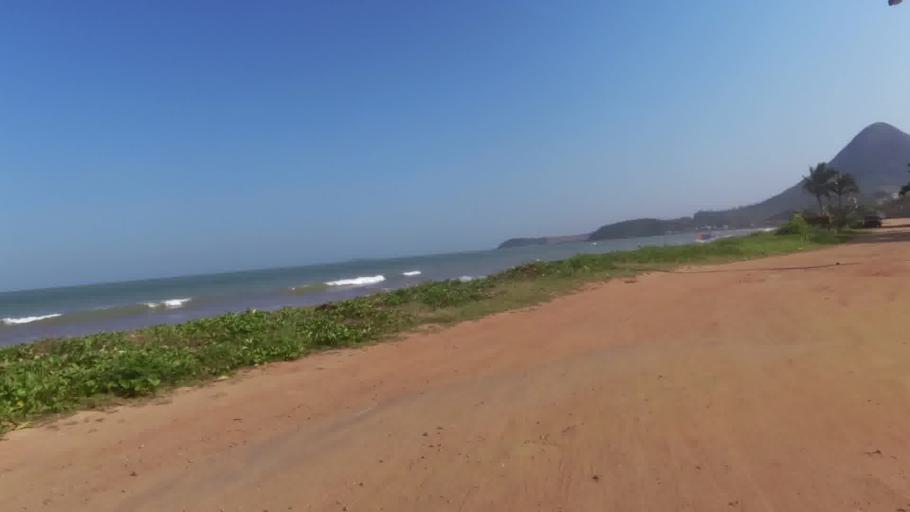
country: BR
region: Espirito Santo
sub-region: Piuma
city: Piuma
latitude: -20.8551
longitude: -40.7509
